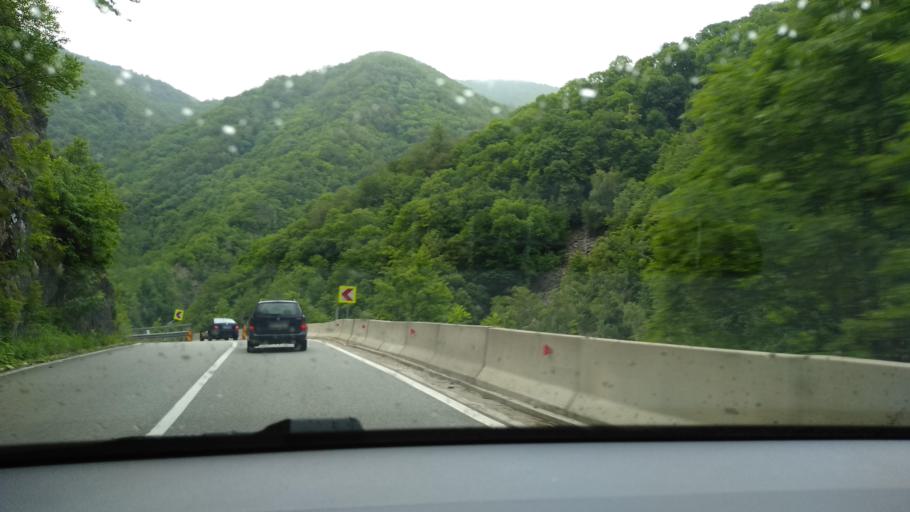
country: RO
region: Hunedoara
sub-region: Comuna Aninoasa
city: Iscroni
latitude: 45.3188
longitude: 23.3749
